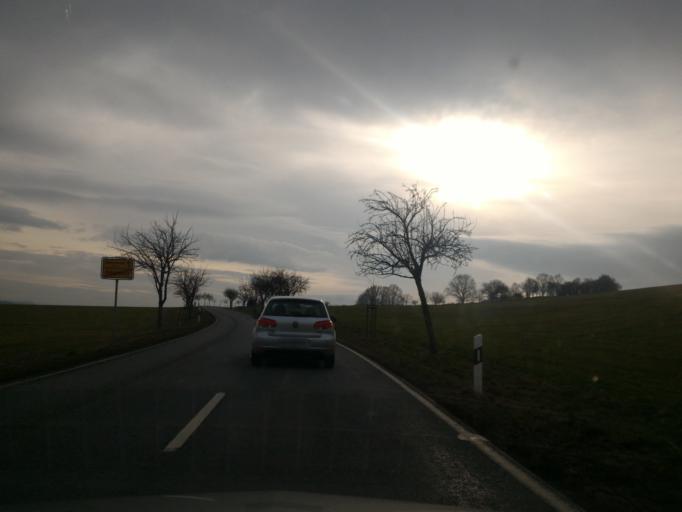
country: DE
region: Saxony
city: Eibau
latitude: 50.9644
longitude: 14.7010
